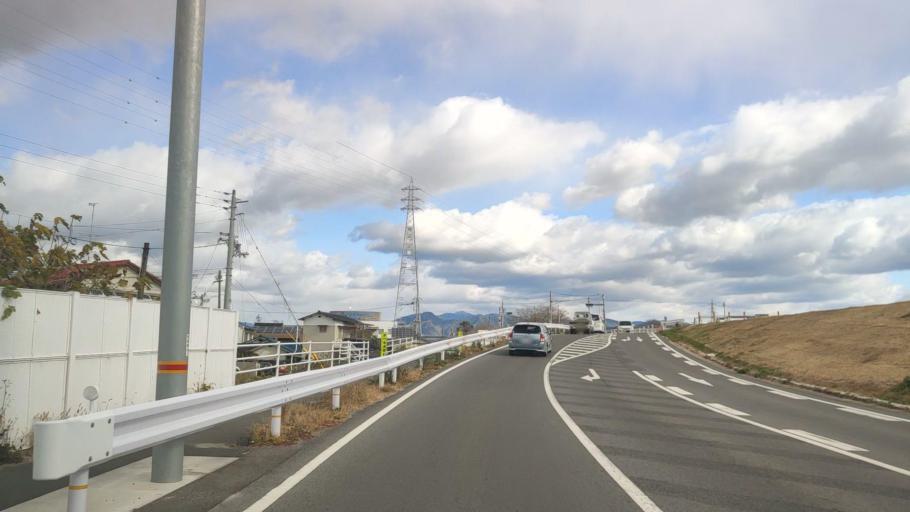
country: JP
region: Ehime
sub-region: Shikoku-chuo Shi
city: Matsuyama
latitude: 33.8153
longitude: 132.7507
